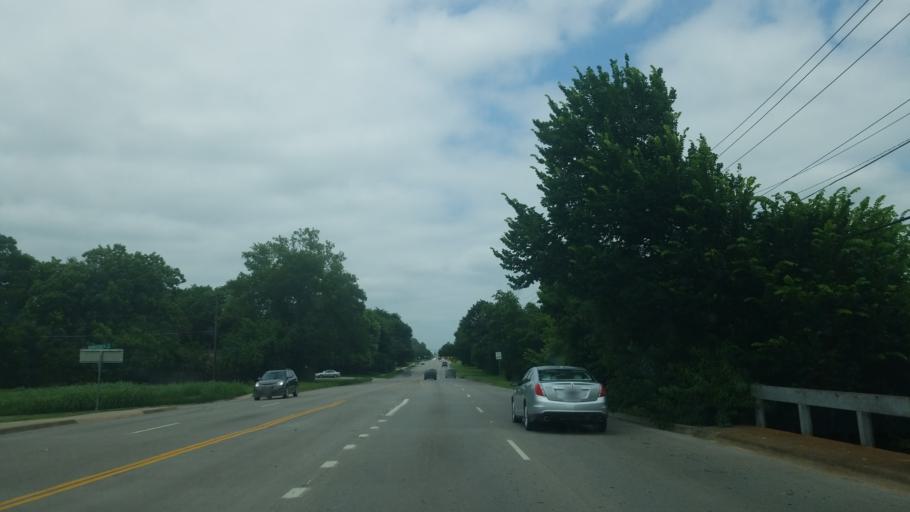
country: US
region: Texas
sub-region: Denton County
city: Denton
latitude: 33.2459
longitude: -97.1180
